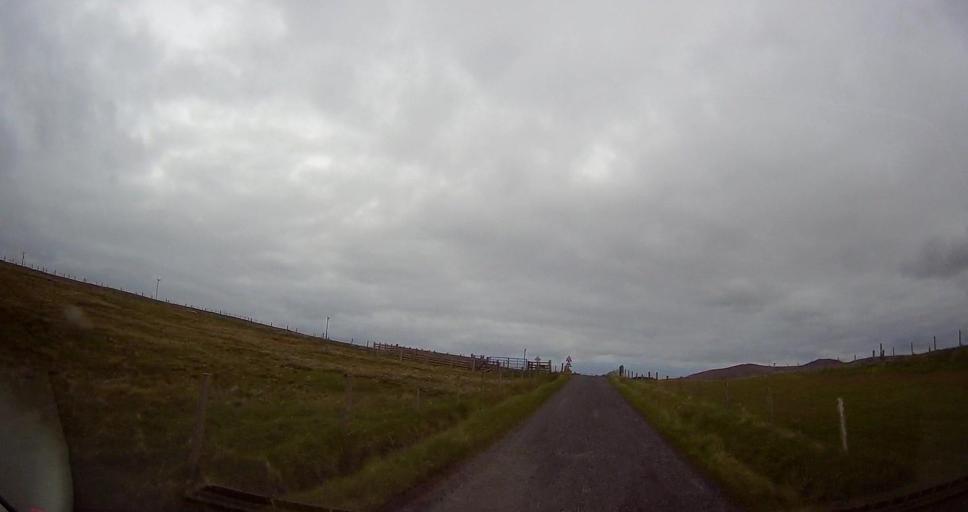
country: GB
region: Scotland
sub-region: Shetland Islands
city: Shetland
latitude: 60.7997
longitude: -0.8727
